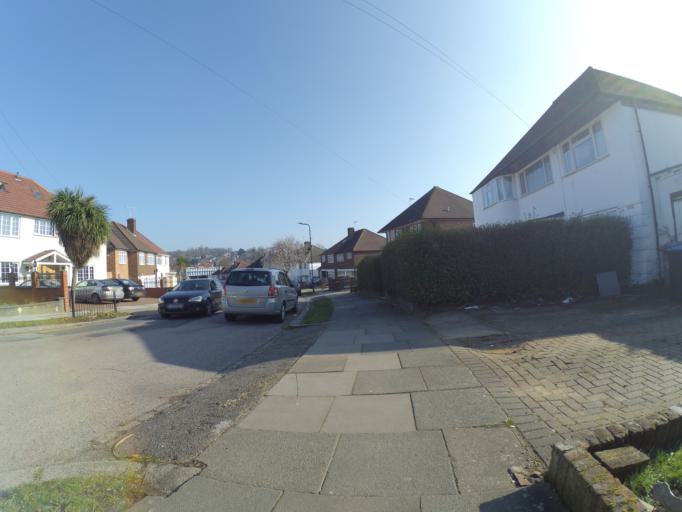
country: GB
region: England
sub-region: Greater London
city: Wembley
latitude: 51.5717
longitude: -0.2924
